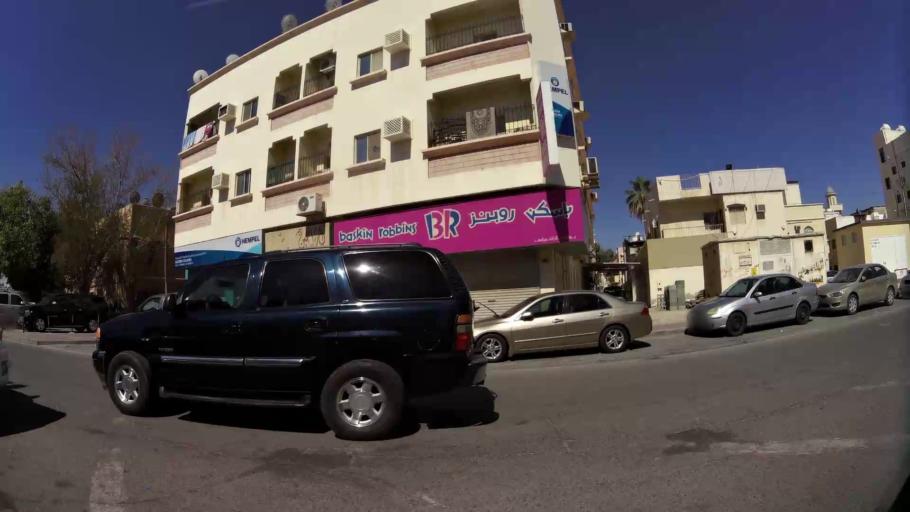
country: BH
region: Muharraq
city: Al Muharraq
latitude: 26.2508
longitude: 50.6187
